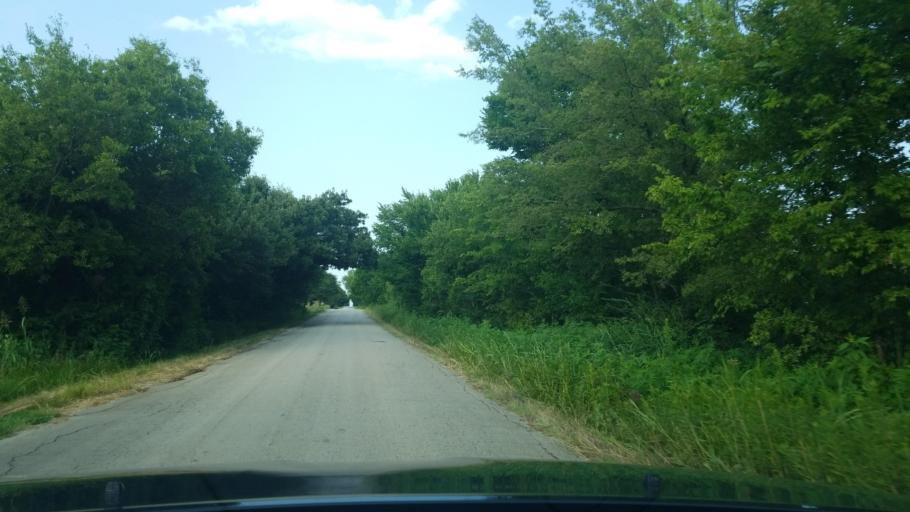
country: US
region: Texas
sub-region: Denton County
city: Denton
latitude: 33.2434
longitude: -97.0705
